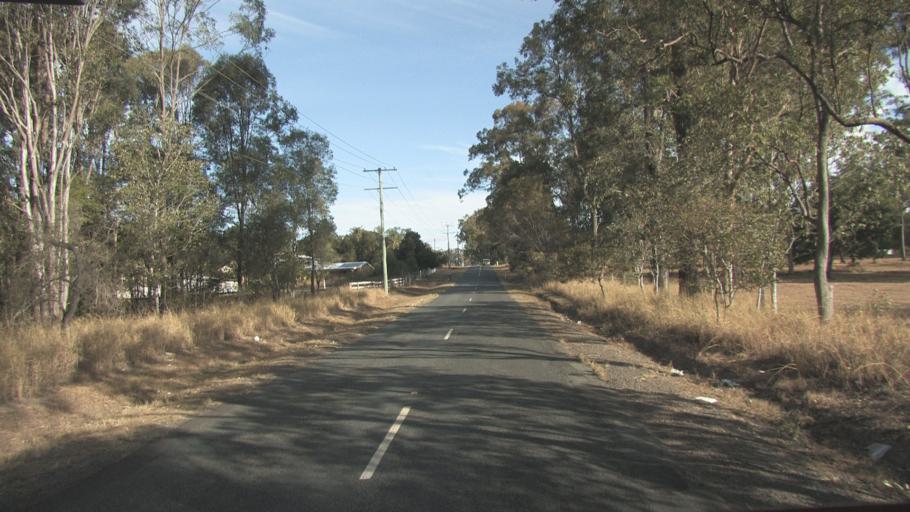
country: AU
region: Queensland
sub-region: Logan
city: Cedar Vale
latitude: -27.8704
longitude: 153.0109
